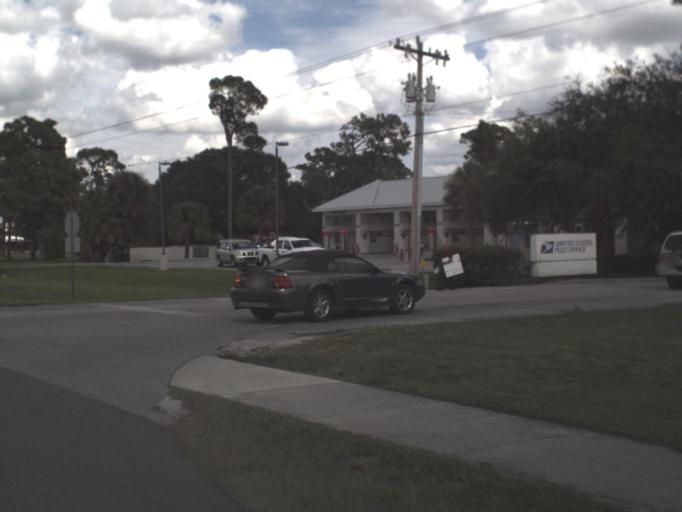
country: US
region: Florida
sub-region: Collier County
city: Immokalee
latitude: 26.4291
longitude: -81.4337
